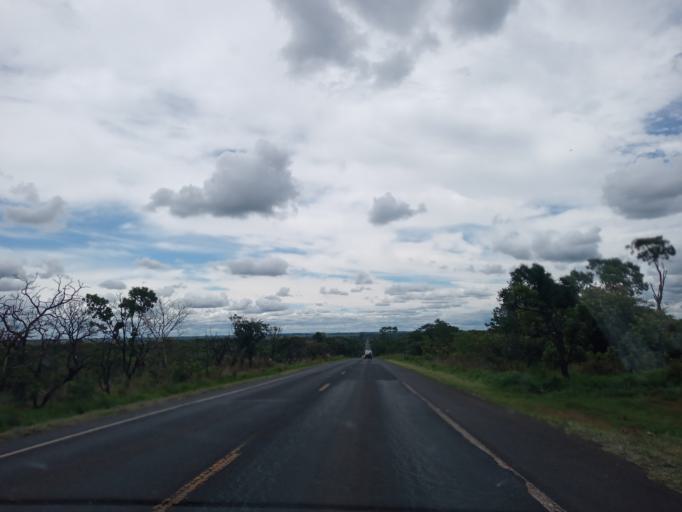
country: BR
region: Minas Gerais
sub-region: Uberlandia
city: Uberlandia
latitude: -19.1881
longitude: -47.8715
